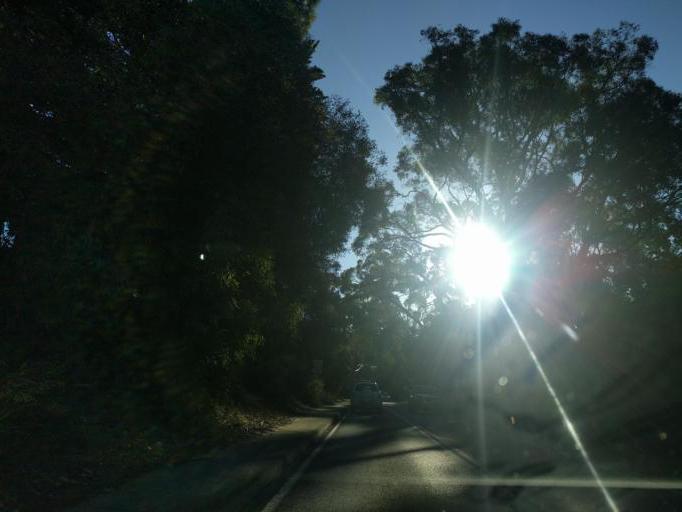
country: AU
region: South Australia
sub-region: Adelaide Hills
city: Aldgate
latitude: -35.0139
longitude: 138.7336
